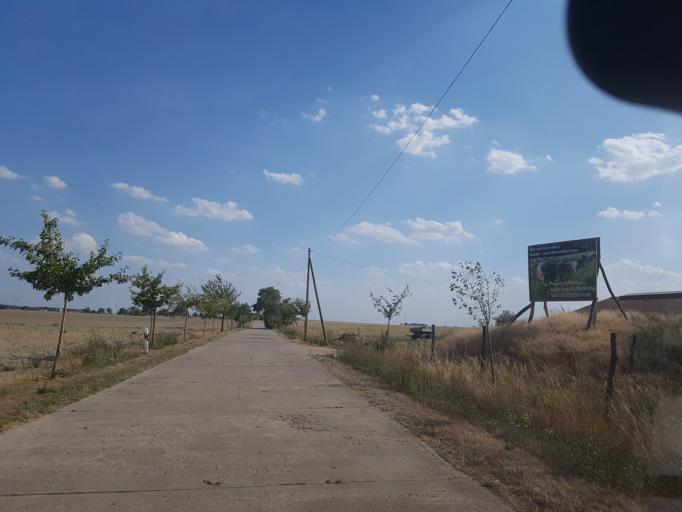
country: DE
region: Brandenburg
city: Niedergorsdorf
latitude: 52.0078
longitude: 12.9256
